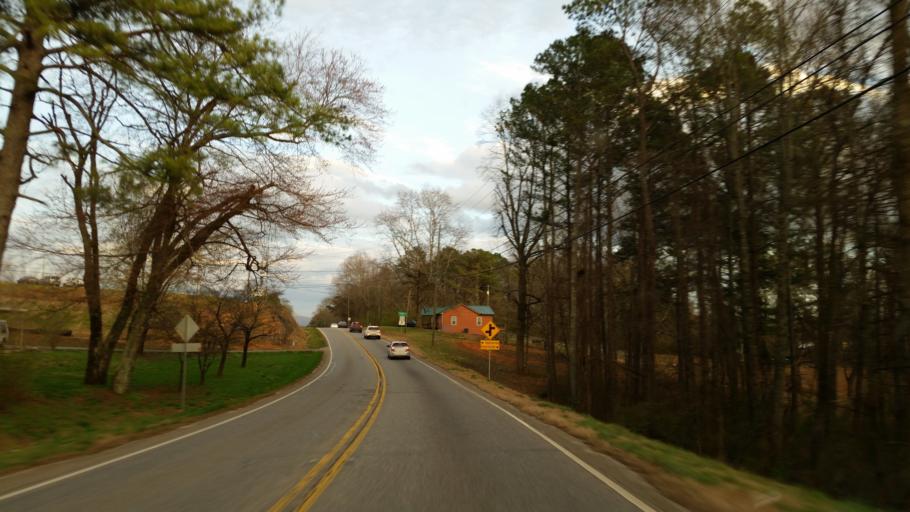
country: US
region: Georgia
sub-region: Pickens County
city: Jasper
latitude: 34.4646
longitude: -84.4766
